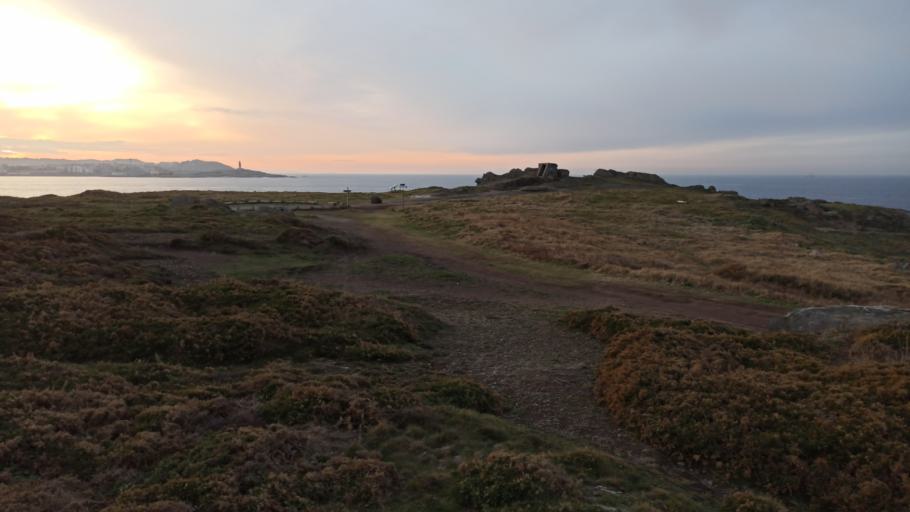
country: ES
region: Galicia
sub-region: Provincia da Coruna
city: A Coruna
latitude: 43.3957
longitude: -8.3482
